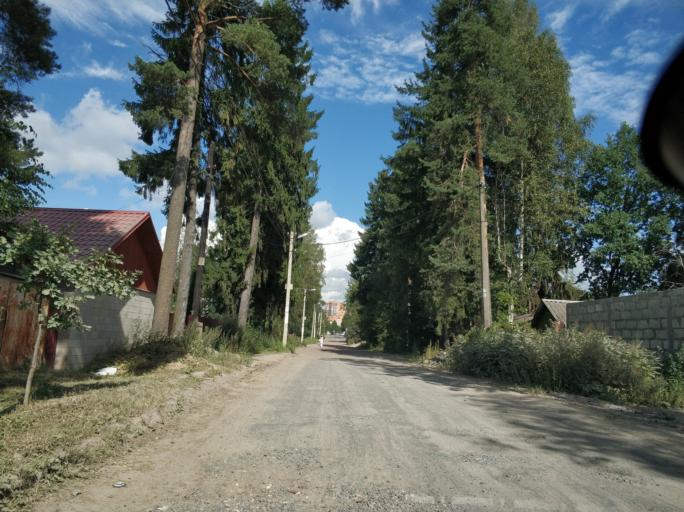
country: RU
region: Leningrad
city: Vsevolozhsk
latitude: 60.0213
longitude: 30.6184
